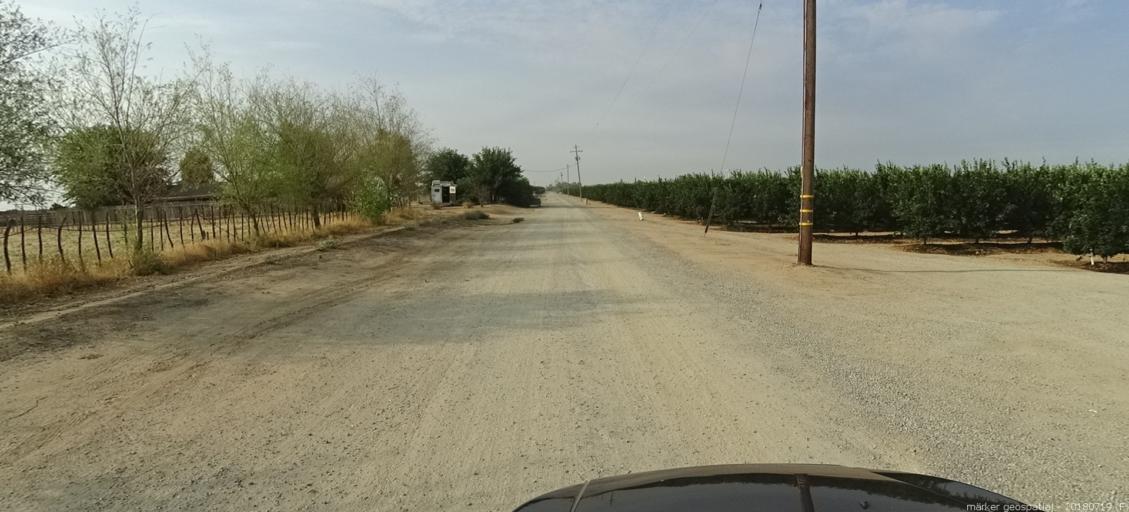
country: US
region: California
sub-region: Madera County
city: Fairmead
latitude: 37.1059
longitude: -120.1931
